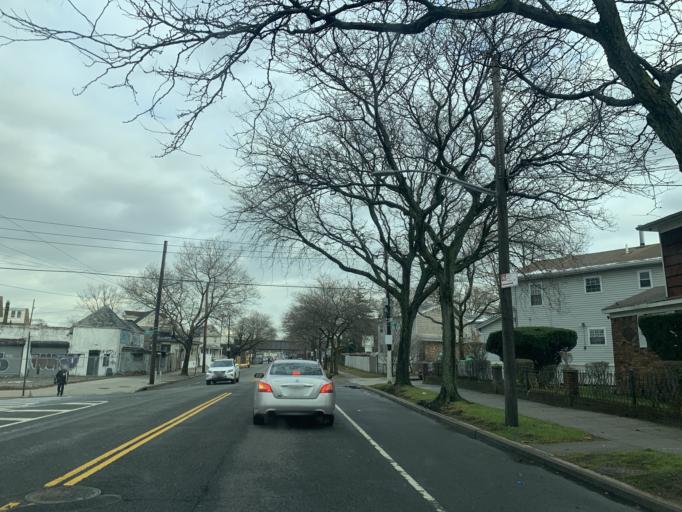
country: US
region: New York
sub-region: Queens County
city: Jamaica
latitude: 40.6881
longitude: -73.7891
